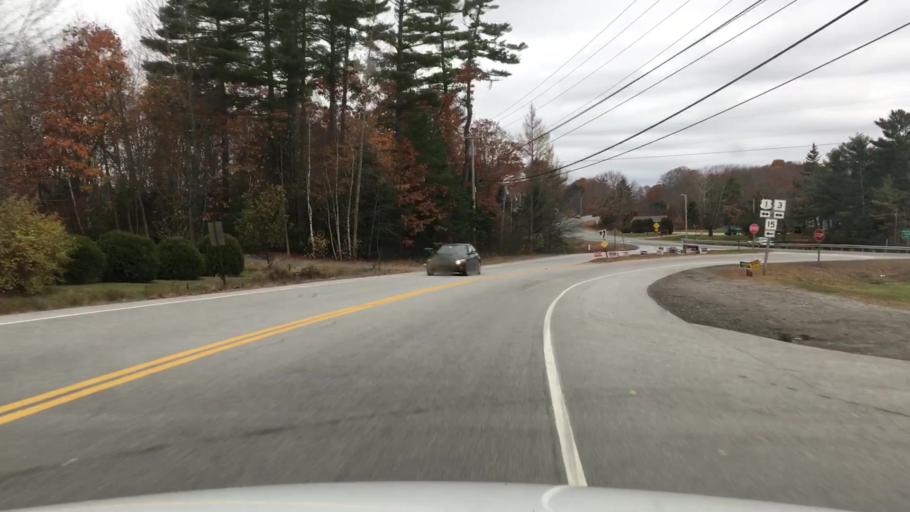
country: US
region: Maine
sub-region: Hancock County
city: Orland
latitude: 44.5595
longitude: -68.7087
